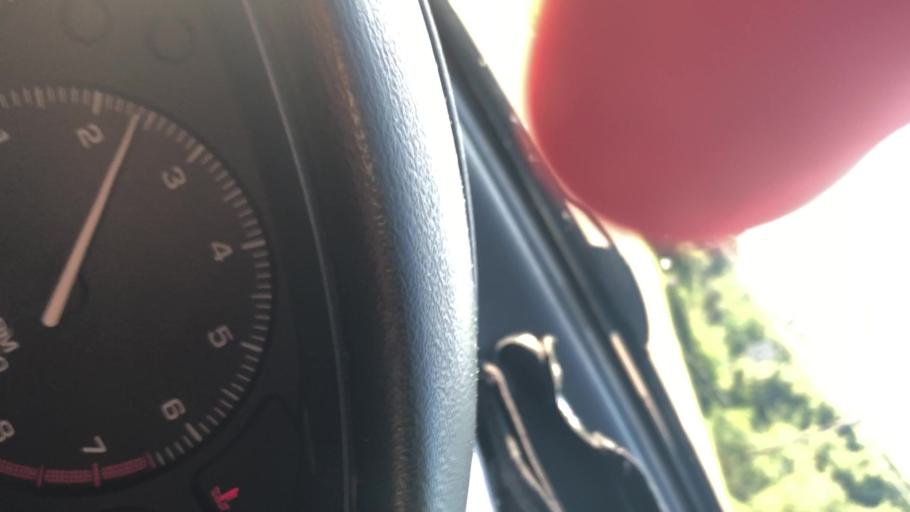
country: US
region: Tennessee
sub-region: Jefferson County
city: Dandridge
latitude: 36.0560
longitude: -83.4686
